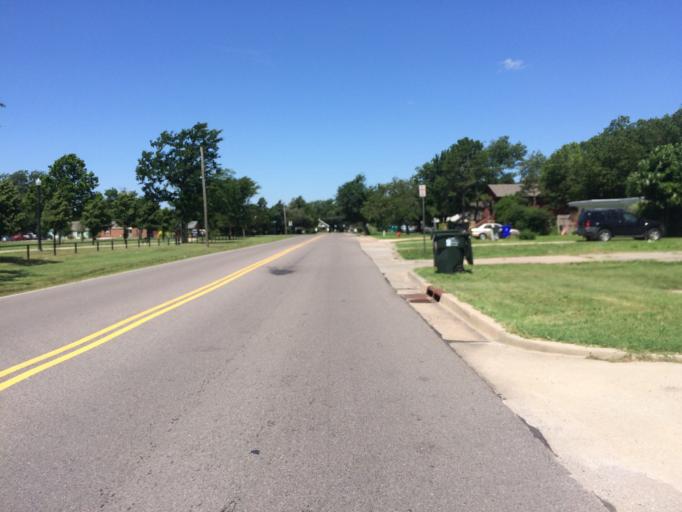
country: US
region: Oklahoma
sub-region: Cleveland County
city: Norman
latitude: 35.2255
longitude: -97.4477
